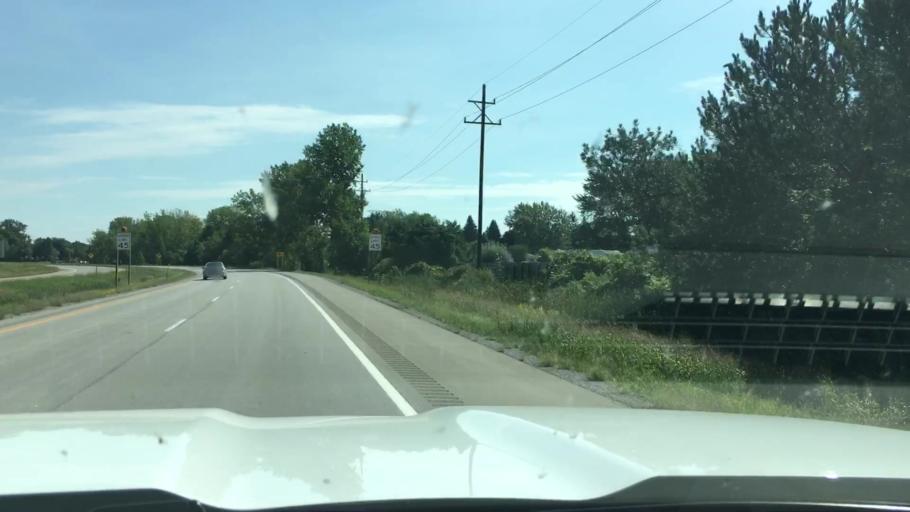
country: US
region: Michigan
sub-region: Bay County
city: Bay City
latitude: 43.5965
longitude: -83.9296
